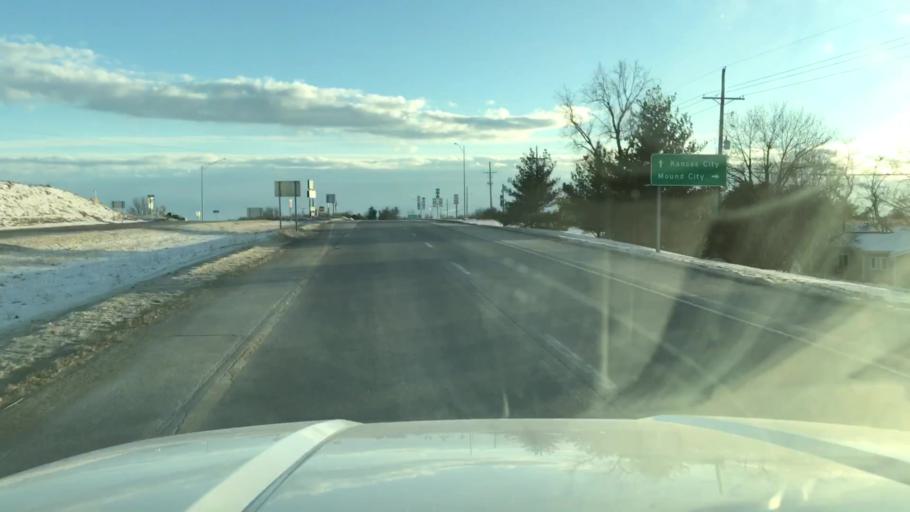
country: US
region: Missouri
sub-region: Andrew County
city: Country Club Village
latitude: 39.8609
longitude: -94.8099
